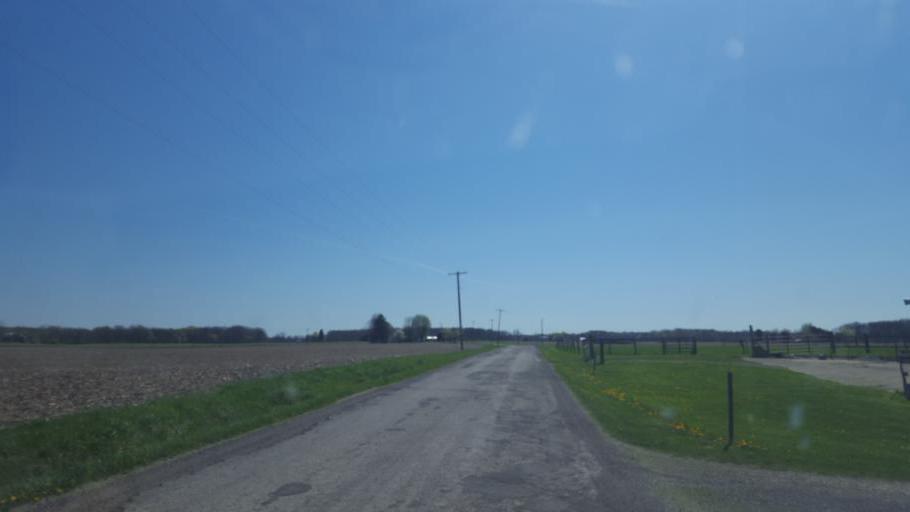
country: US
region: Ohio
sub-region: Morrow County
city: Mount Gilead
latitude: 40.6116
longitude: -82.8667
